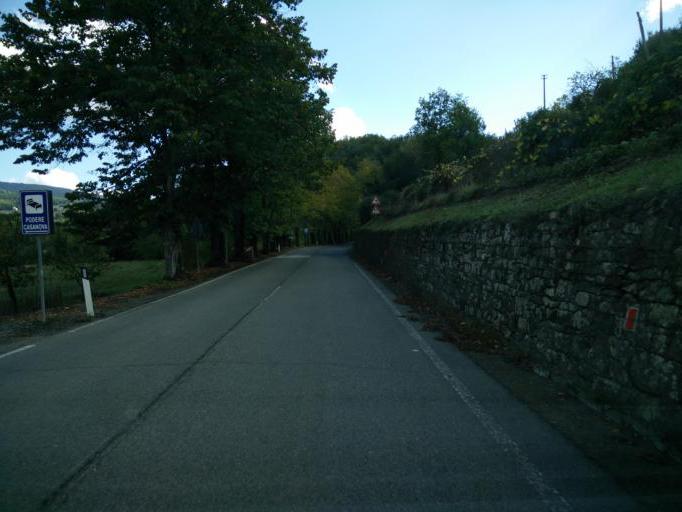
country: IT
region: Tuscany
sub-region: Province of Florence
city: Greve in Chianti
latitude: 43.5713
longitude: 11.3199
